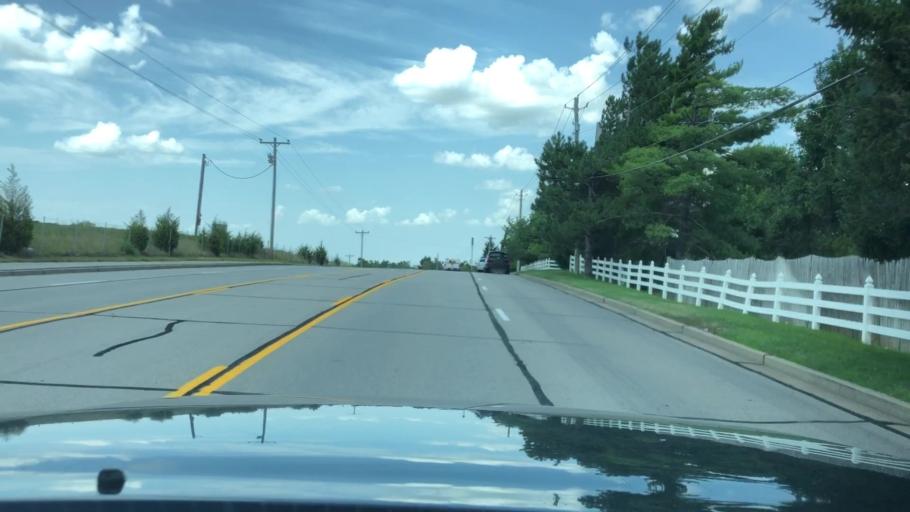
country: US
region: Missouri
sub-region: Saint Charles County
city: O'Fallon
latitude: 38.7901
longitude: -90.6810
